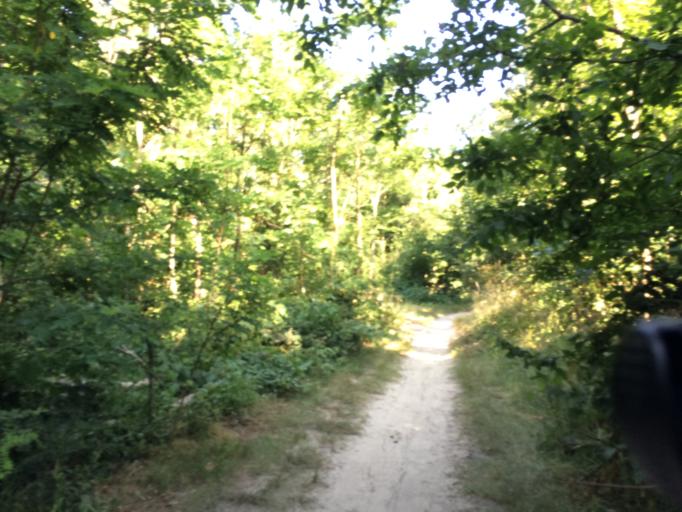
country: FR
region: Ile-de-France
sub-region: Departement de l'Essonne
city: Soisy-sur-Seine
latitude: 48.6589
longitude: 2.4661
